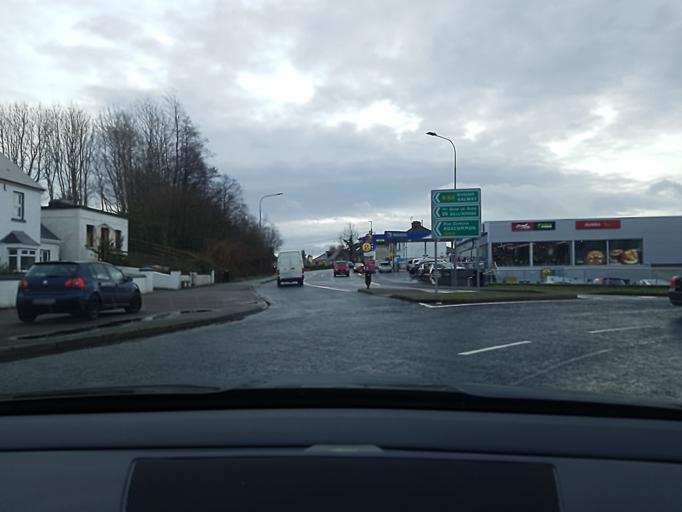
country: IE
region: Connaught
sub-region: Maigh Eo
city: Castlebar
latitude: 53.8519
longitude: -9.2932
